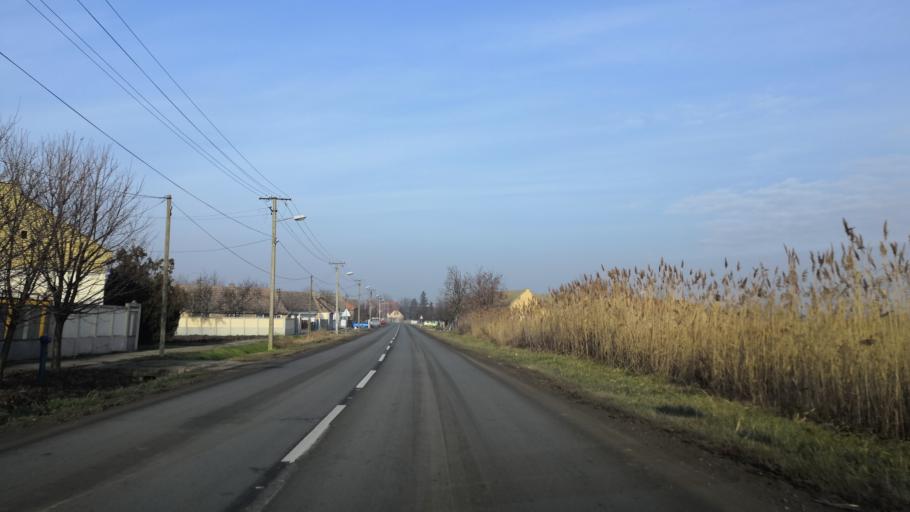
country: RS
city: Kisac
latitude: 45.3435
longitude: 19.7338
